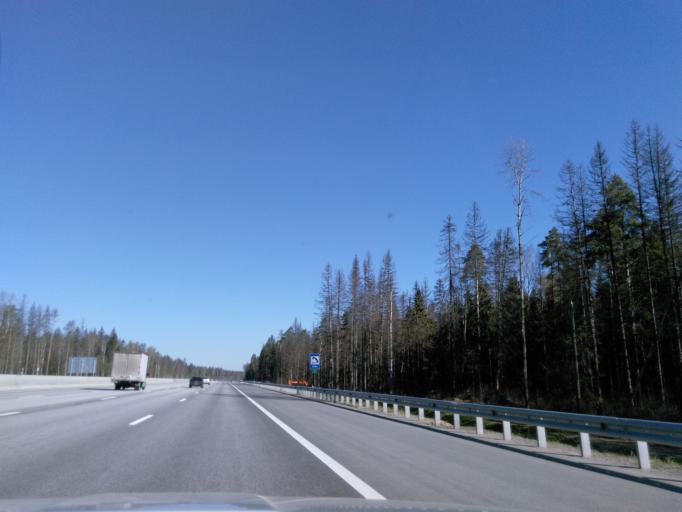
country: RU
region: Moskovskaya
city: Rzhavki
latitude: 56.0163
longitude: 37.2816
